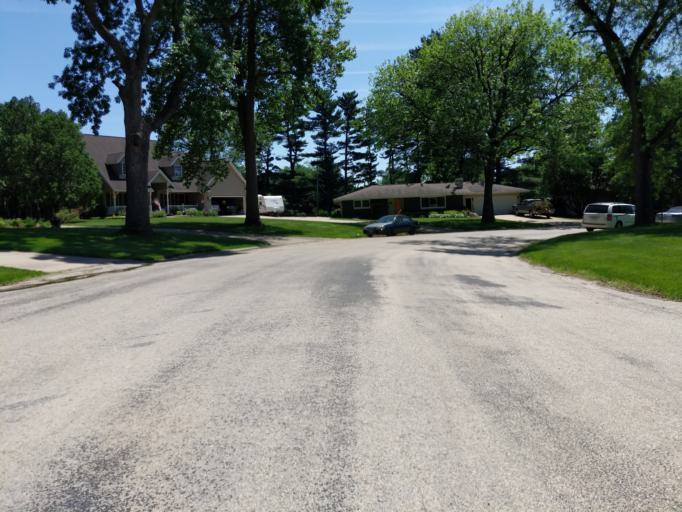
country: US
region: Iowa
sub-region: Linn County
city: Cedar Rapids
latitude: 42.0231
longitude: -91.6402
